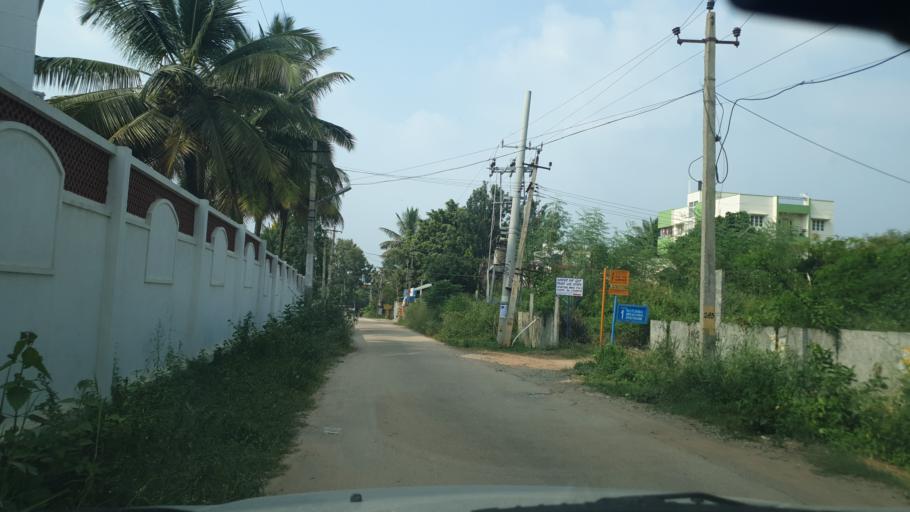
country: IN
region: Karnataka
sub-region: Bangalore Urban
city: Yelahanka
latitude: 13.0681
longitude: 77.6598
